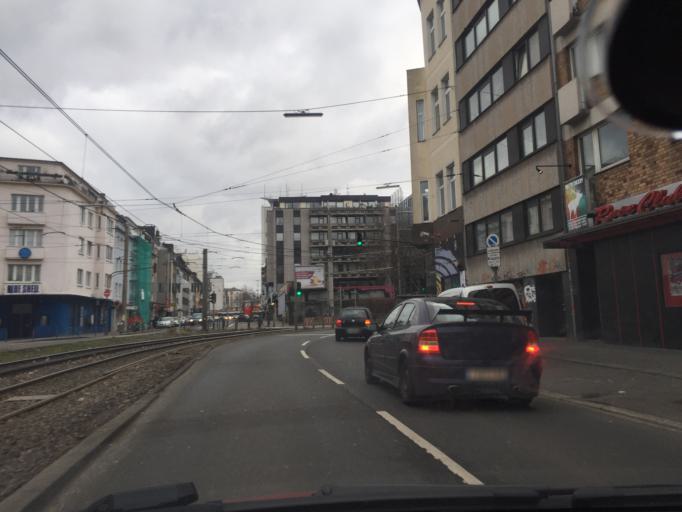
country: DE
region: North Rhine-Westphalia
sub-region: Regierungsbezirk Koln
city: Neustadt/Sued
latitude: 50.9272
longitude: 6.9396
